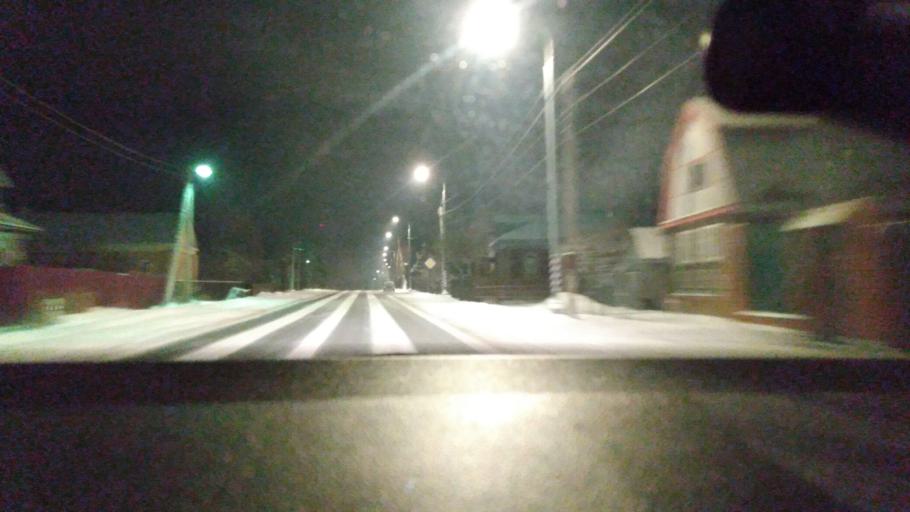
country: RU
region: Moskovskaya
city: Krasnaya Poyma
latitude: 55.1026
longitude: 38.9943
